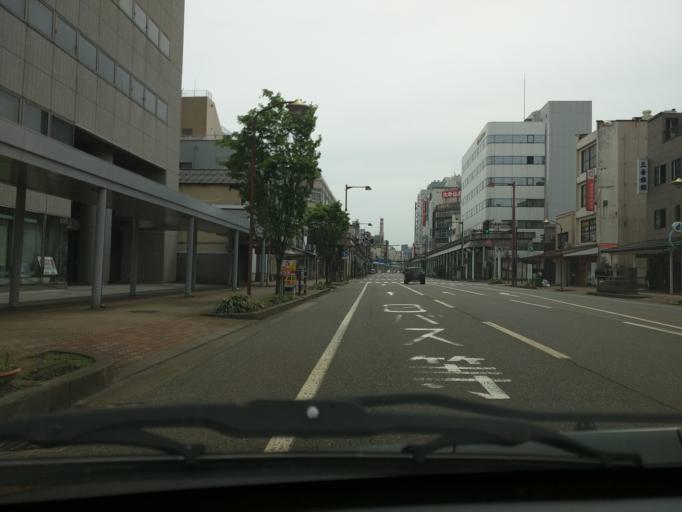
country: JP
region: Niigata
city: Nagaoka
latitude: 37.4505
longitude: 138.8518
